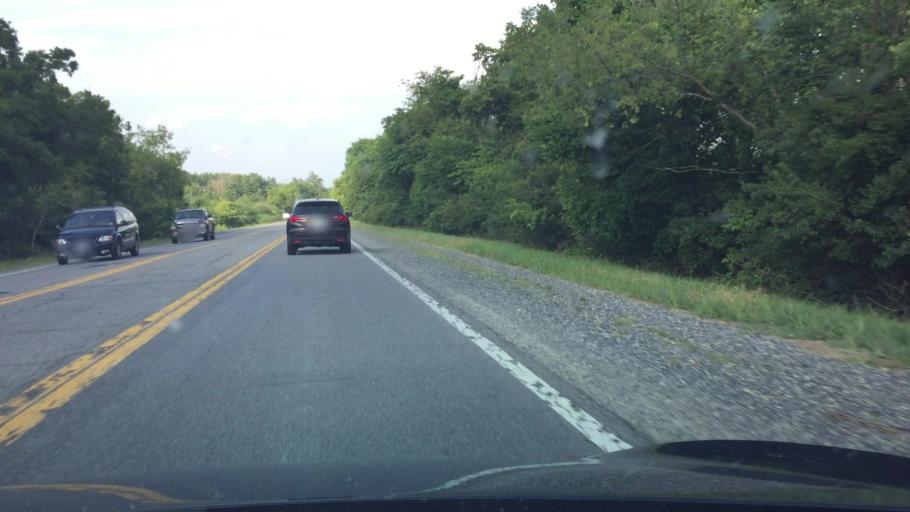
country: US
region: Virginia
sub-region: Pulaski County
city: Dublin
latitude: 37.1306
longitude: -80.6354
